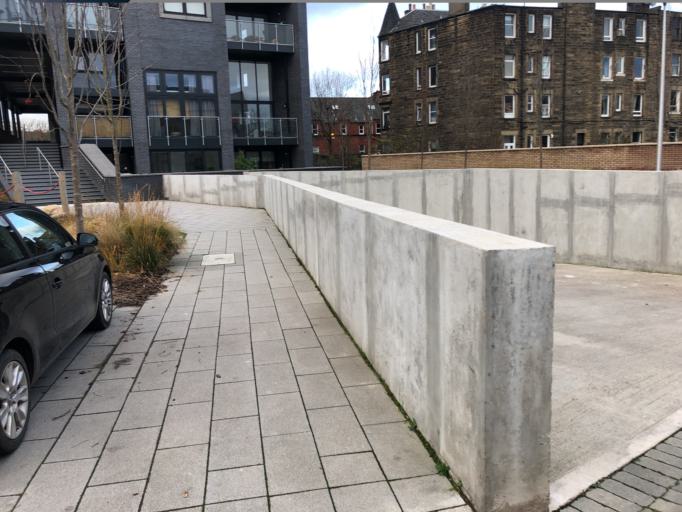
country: GB
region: Scotland
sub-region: West Lothian
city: Seafield
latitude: 55.9603
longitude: -3.1678
